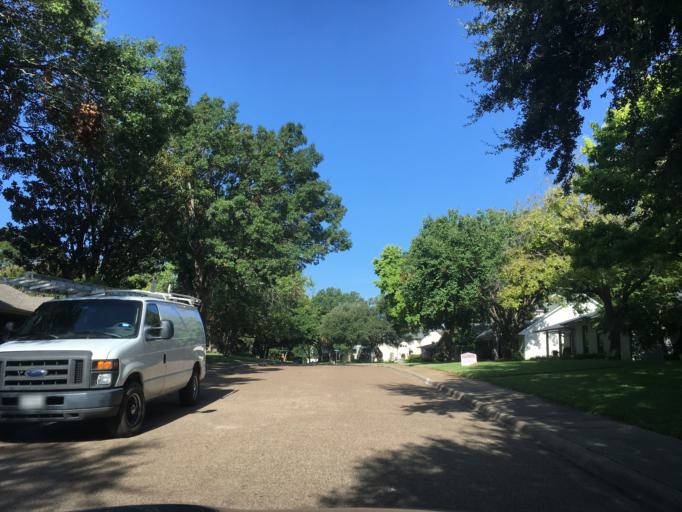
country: US
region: Texas
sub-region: Dallas County
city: Richardson
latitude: 32.8830
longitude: -96.7224
